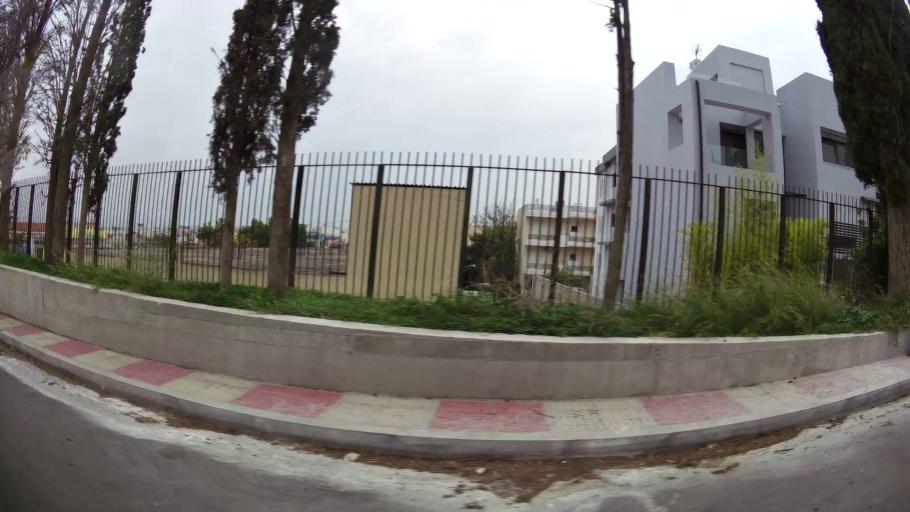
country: GR
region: Attica
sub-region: Nomarchia Athinas
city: Marousi
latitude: 38.0460
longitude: 23.7846
